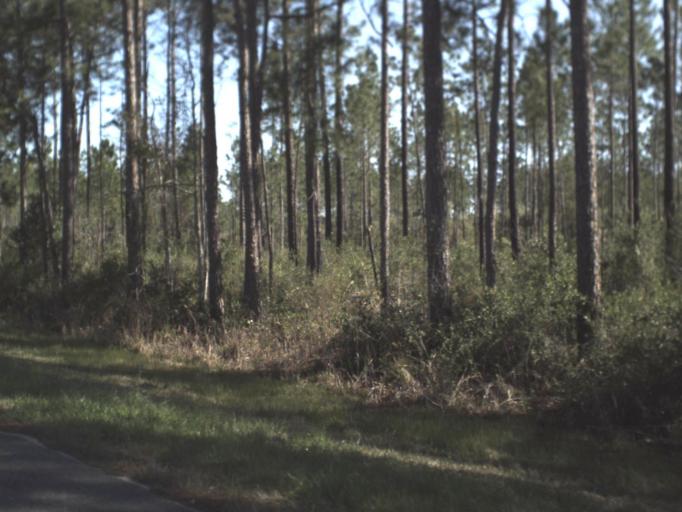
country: US
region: Florida
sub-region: Leon County
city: Woodville
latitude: 30.2407
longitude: -84.0427
